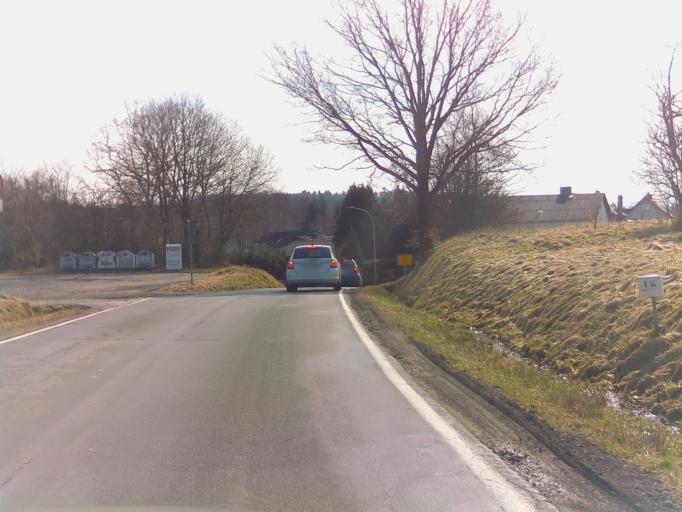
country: DE
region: Hesse
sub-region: Regierungsbezirk Giessen
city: Grunberg
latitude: 50.6250
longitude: 9.0241
